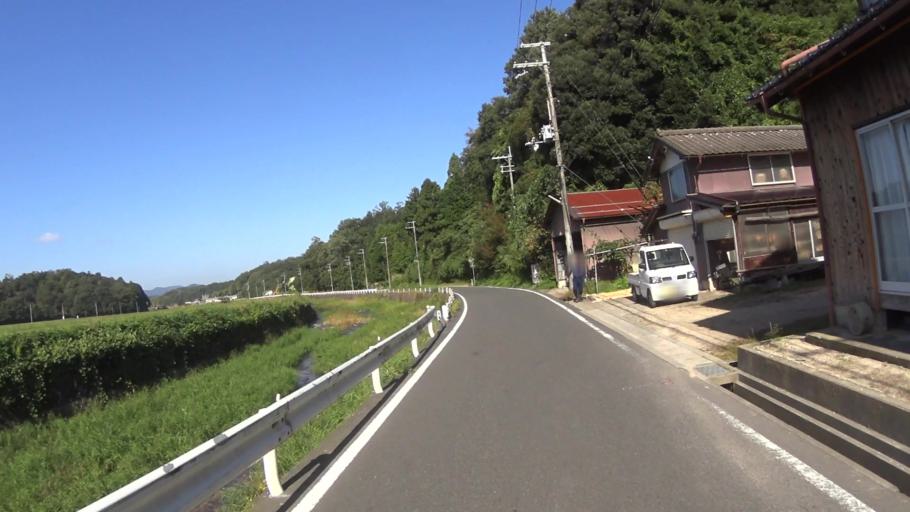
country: JP
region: Kyoto
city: Miyazu
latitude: 35.6586
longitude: 135.1106
